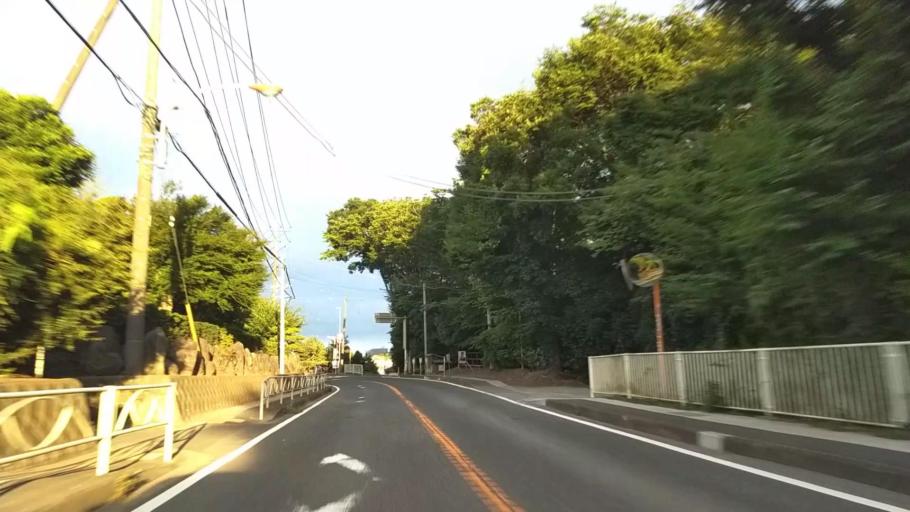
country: JP
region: Kanagawa
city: Atsugi
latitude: 35.4710
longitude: 139.3162
